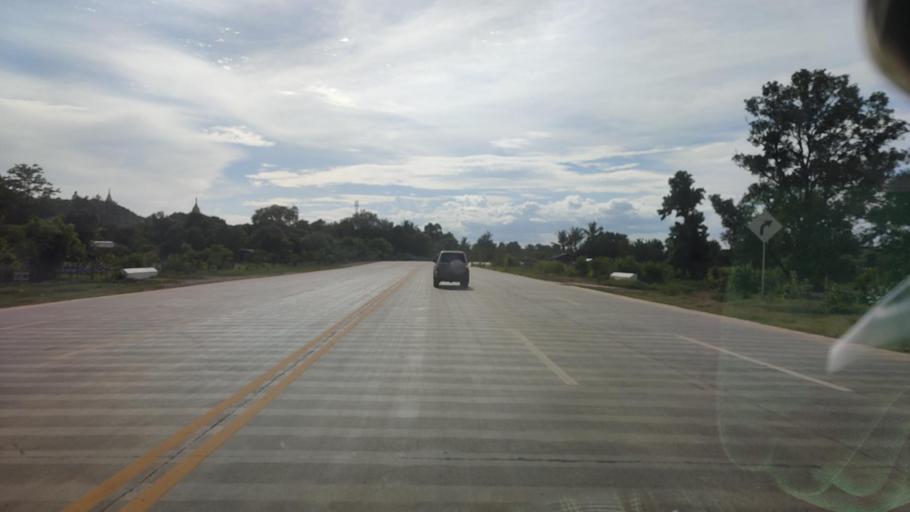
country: MM
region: Mandalay
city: Kyaukse
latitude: 21.6104
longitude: 96.1572
